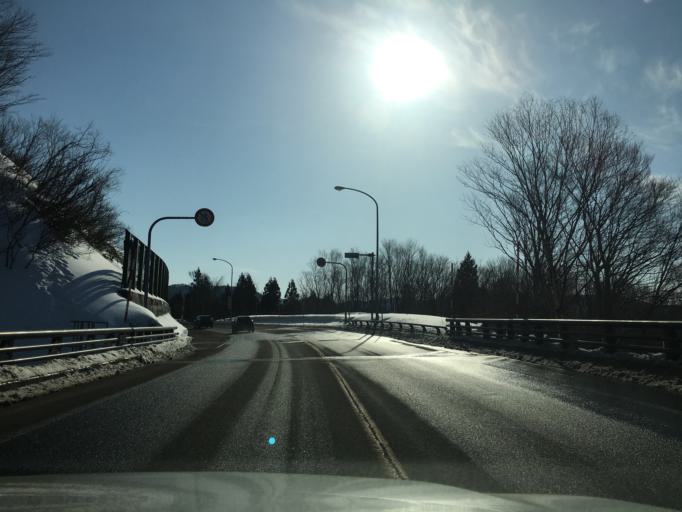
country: JP
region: Yamagata
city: Tsuruoka
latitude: 38.5693
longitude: 139.9373
